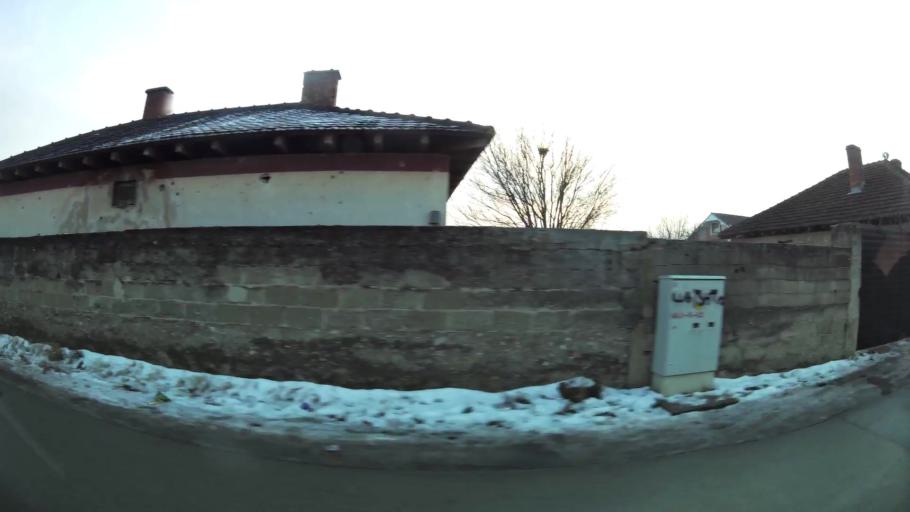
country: MK
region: Aracinovo
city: Arachinovo
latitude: 42.0241
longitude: 21.5553
